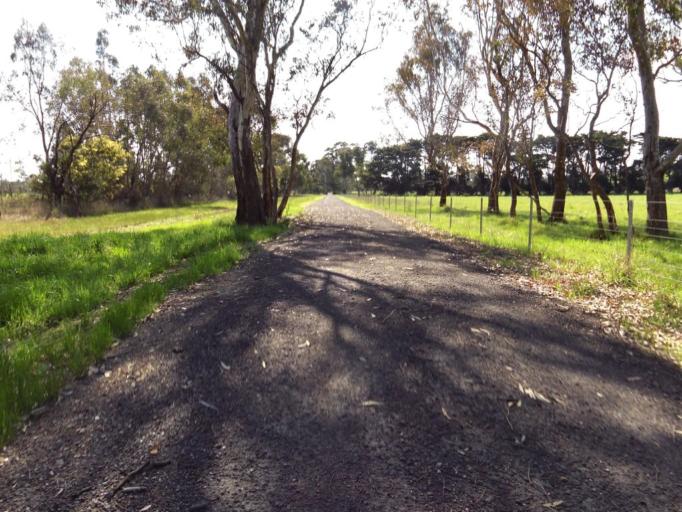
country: AU
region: Victoria
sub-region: Murrindindi
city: Alexandra
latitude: -37.1252
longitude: 145.5988
